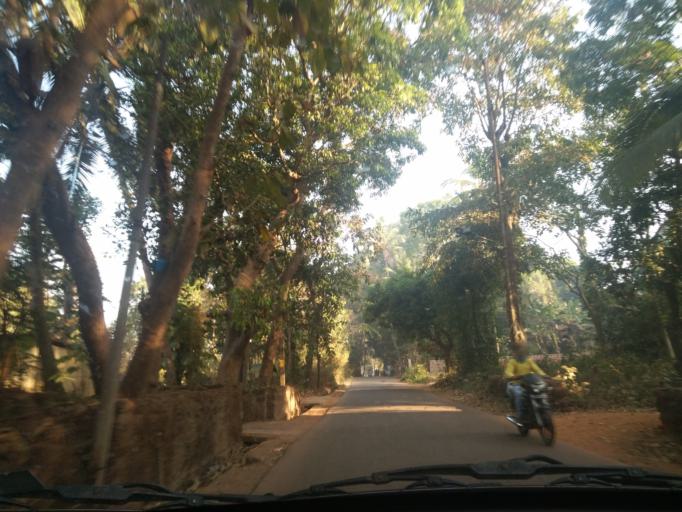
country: IN
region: Goa
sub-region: South Goa
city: Davorlim
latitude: 15.2792
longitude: 74.0060
